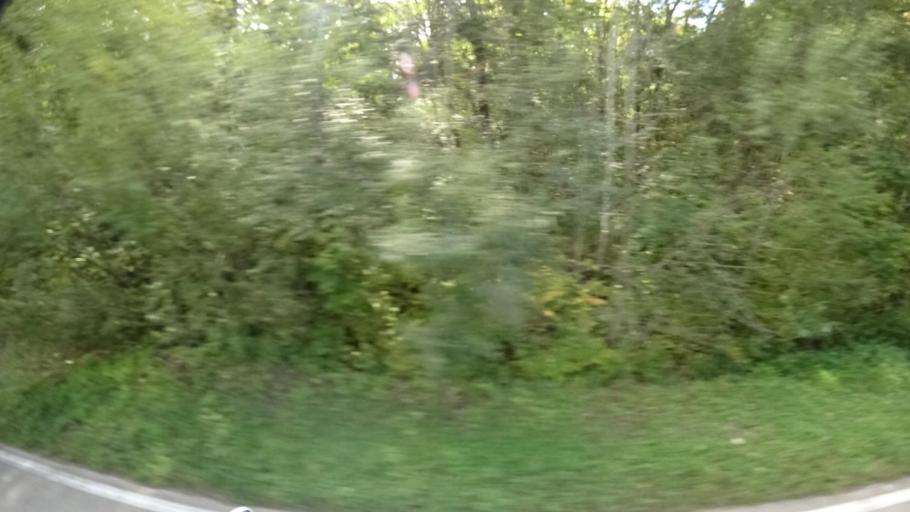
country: RU
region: Primorskiy
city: Yakovlevka
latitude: 44.4023
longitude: 133.5955
